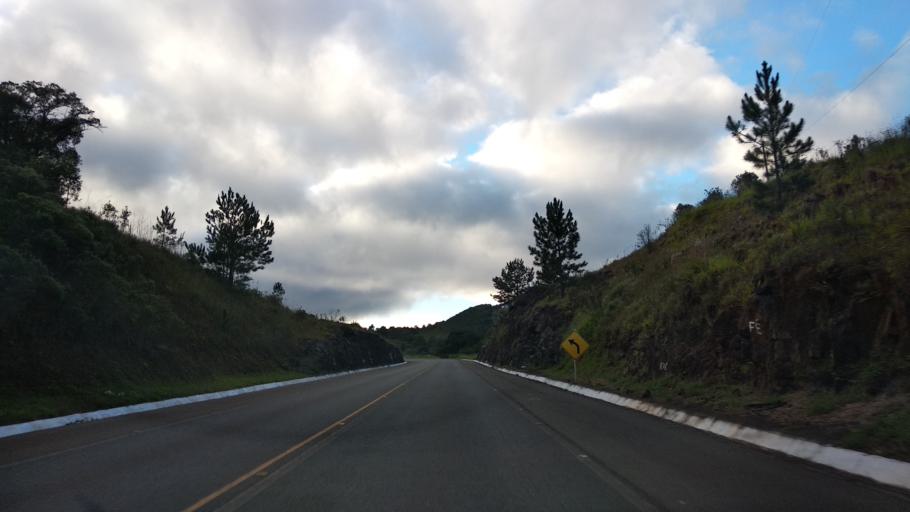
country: BR
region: Santa Catarina
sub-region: Curitibanos
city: Curitibanos
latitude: -27.5684
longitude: -50.8187
